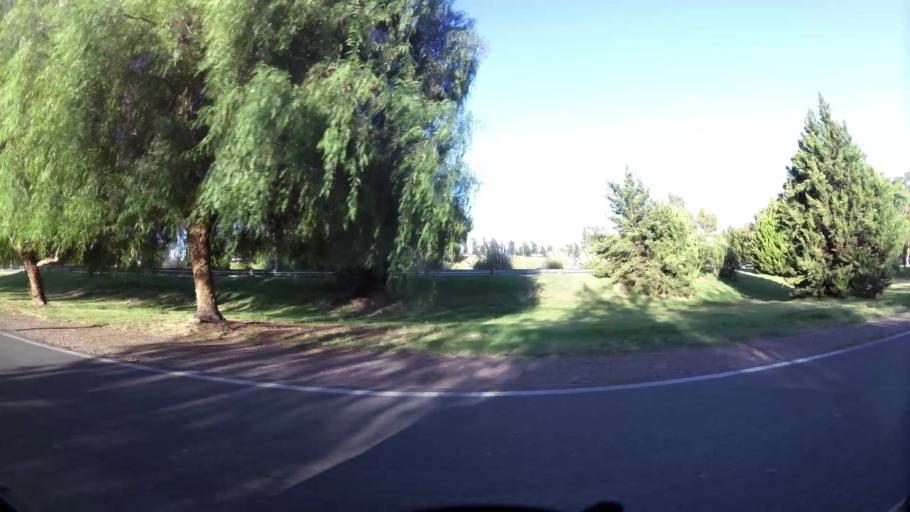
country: AR
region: San Juan
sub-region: Departamento de Santa Lucia
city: Santa Lucia
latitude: -31.5488
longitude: -68.5068
